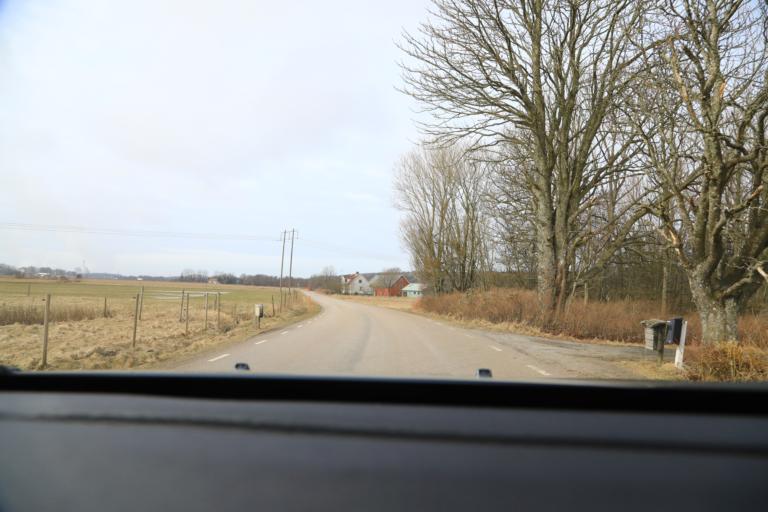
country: SE
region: Halland
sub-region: Varbergs Kommun
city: Veddige
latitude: 57.2281
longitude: 12.2438
